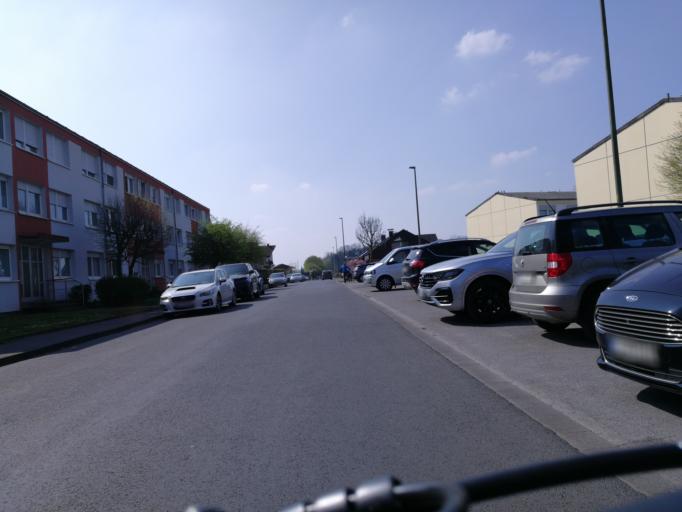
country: DE
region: North Rhine-Westphalia
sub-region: Regierungsbezirk Dusseldorf
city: Dormagen
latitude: 51.1227
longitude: 6.8411
